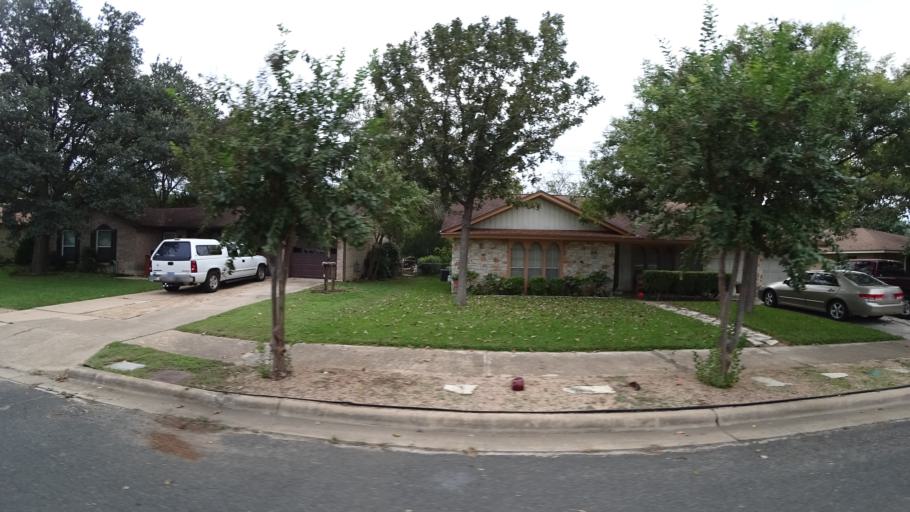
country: US
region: Texas
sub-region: Travis County
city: Rollingwood
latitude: 30.2139
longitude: -97.7890
